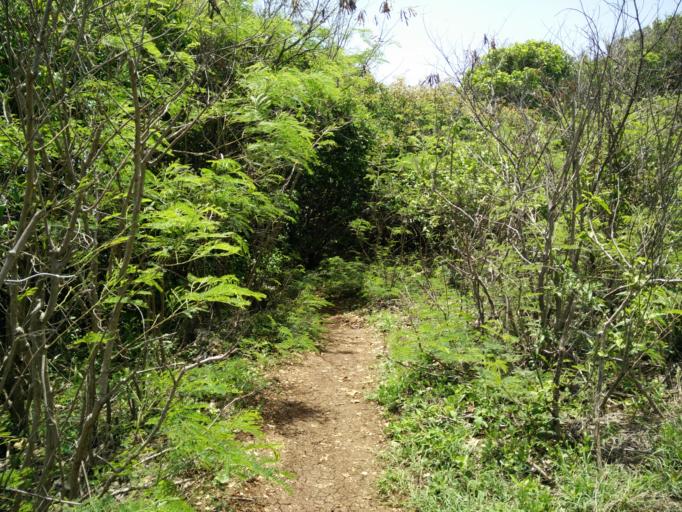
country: GP
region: Guadeloupe
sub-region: Guadeloupe
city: Sainte-Anne
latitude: 16.2400
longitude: -61.3423
